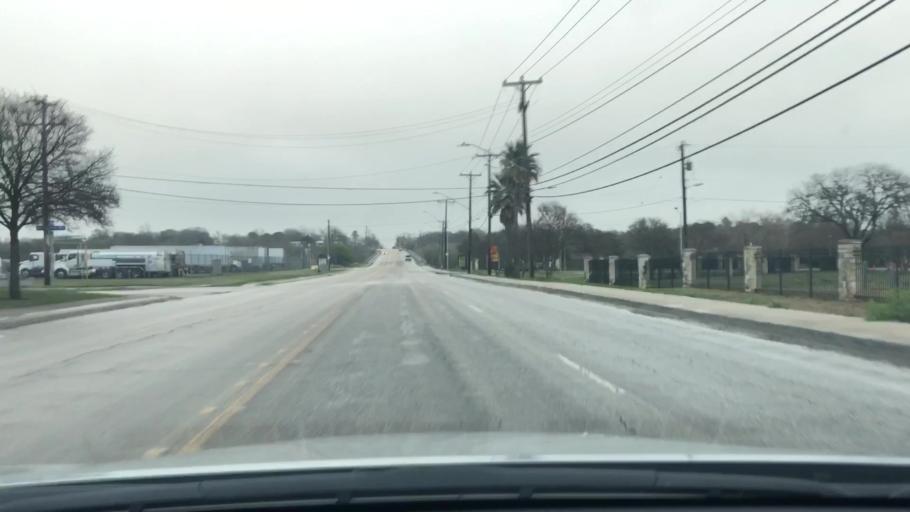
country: US
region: Texas
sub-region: Bexar County
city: Kirby
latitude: 29.4357
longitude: -98.4232
